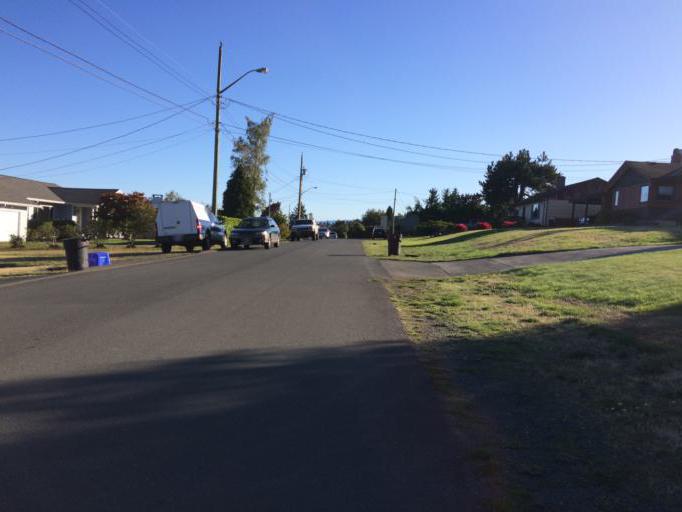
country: CA
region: British Columbia
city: Campbell River
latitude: 50.0140
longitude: -125.2369
